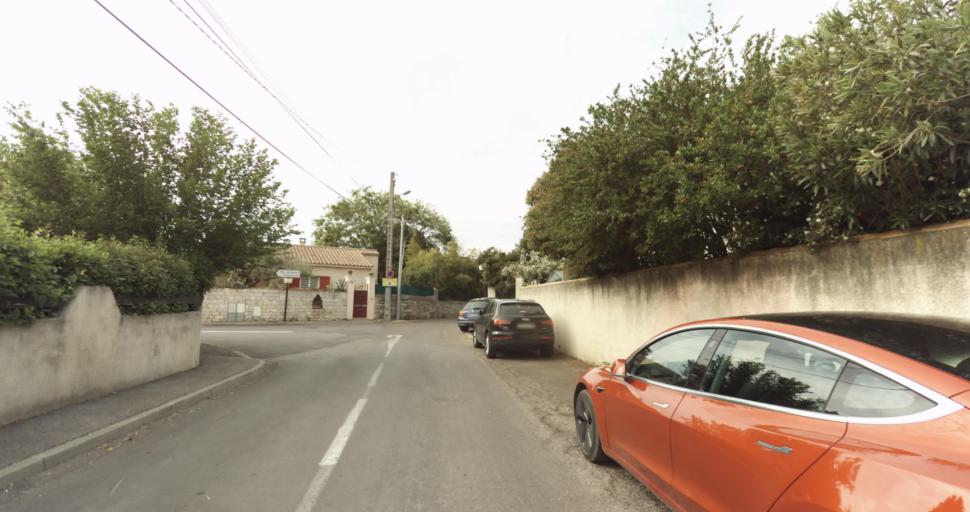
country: FR
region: Languedoc-Roussillon
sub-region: Departement du Gard
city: Nimes
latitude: 43.8154
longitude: 4.3266
